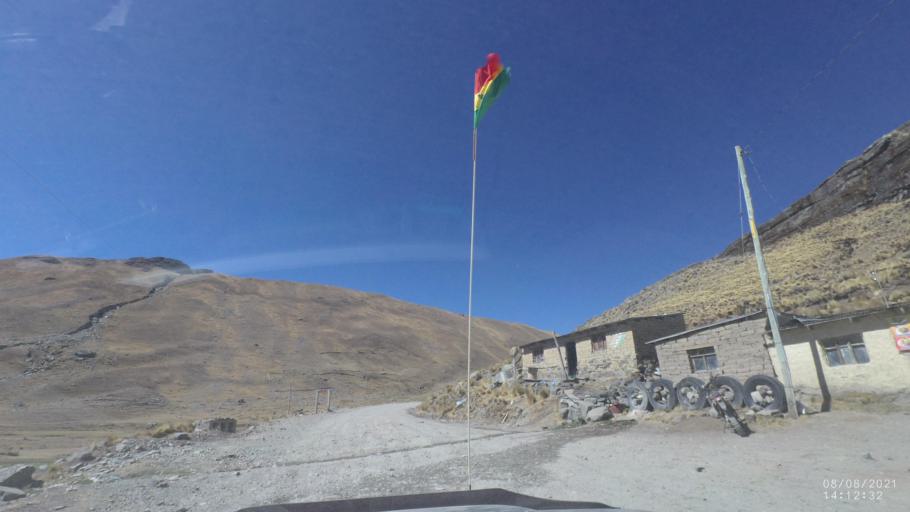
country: BO
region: Cochabamba
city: Sipe Sipe
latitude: -17.1656
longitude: -66.4276
